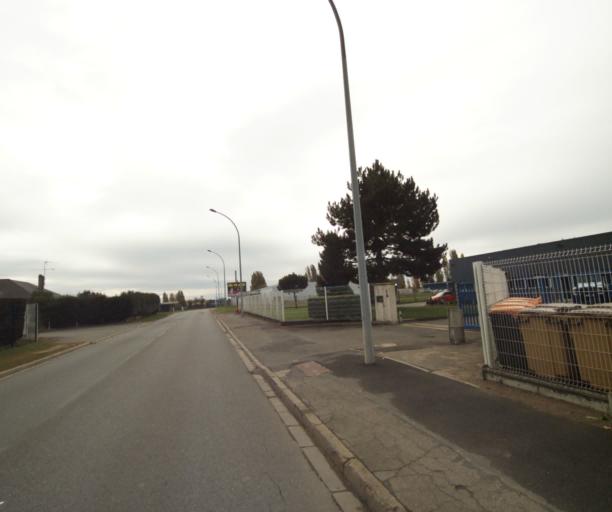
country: FR
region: Centre
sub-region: Departement d'Eure-et-Loir
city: Dreux
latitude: 48.7499
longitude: 1.3618
